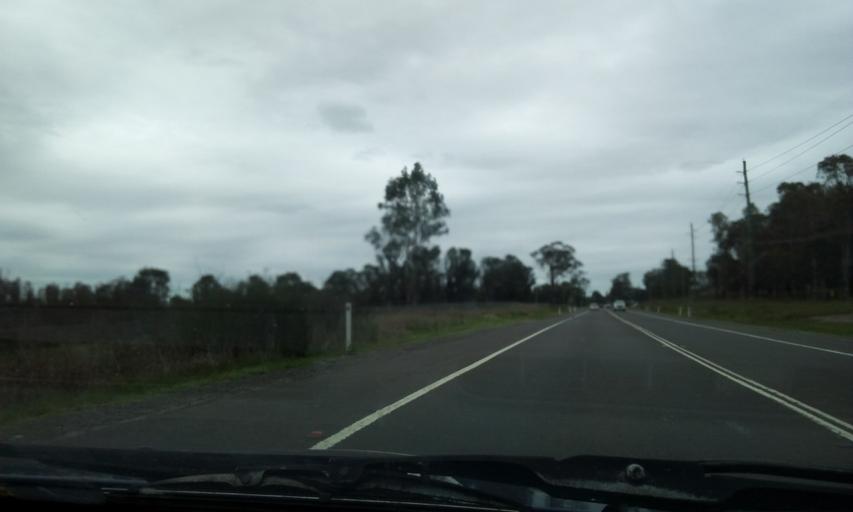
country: AU
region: New South Wales
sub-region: Penrith Municipality
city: Glenmore Park
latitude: -33.8016
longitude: 150.6974
